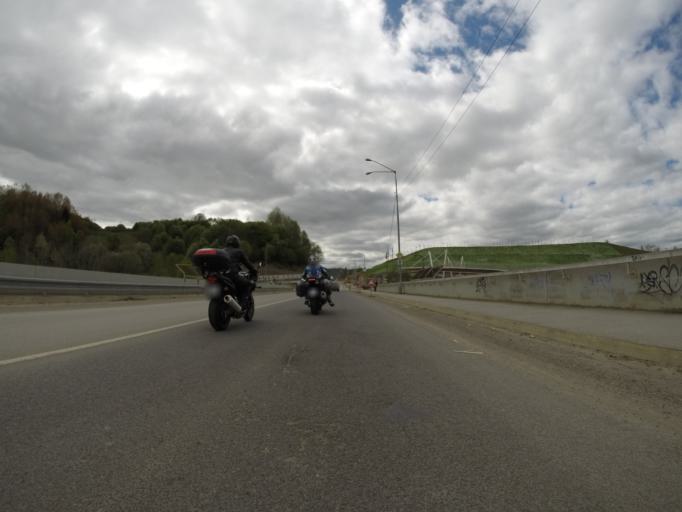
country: SK
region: Banskobystricky
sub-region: Okres Banska Bystrica
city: Brezno
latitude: 48.7987
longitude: 19.6391
